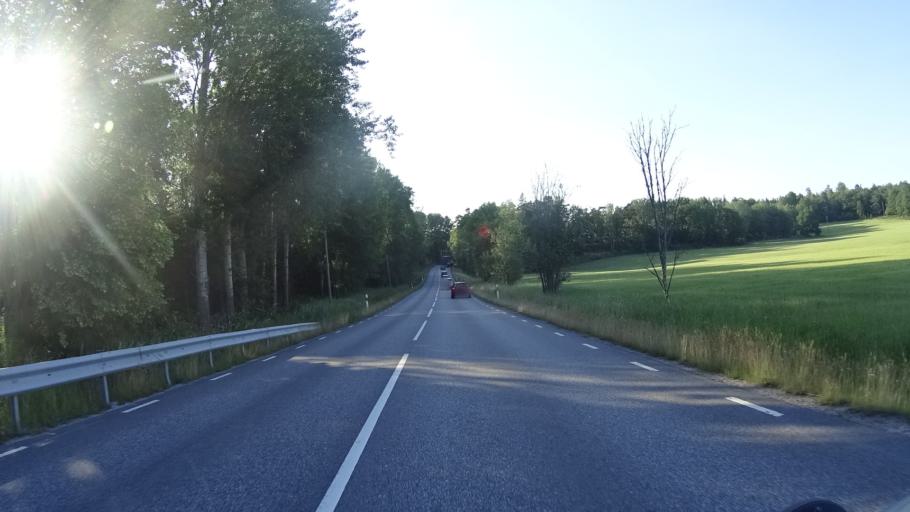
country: SE
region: Stockholm
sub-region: Sodertalje Kommun
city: Pershagen
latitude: 59.1136
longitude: 17.6418
